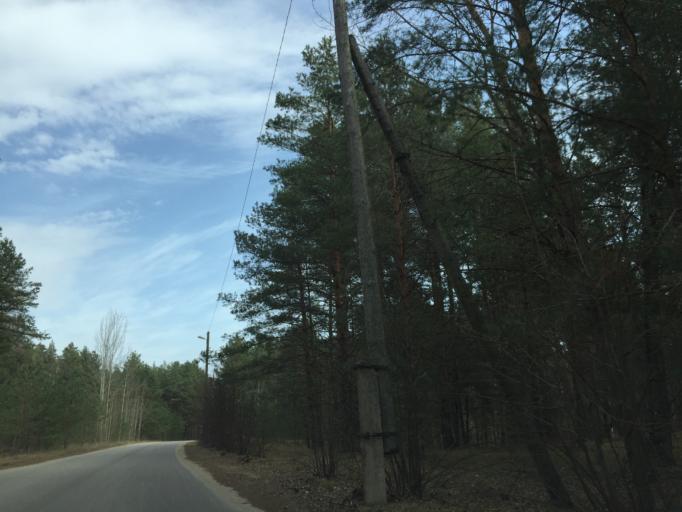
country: LV
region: Daugavpils
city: Daugavpils
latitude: 55.9014
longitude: 26.4684
